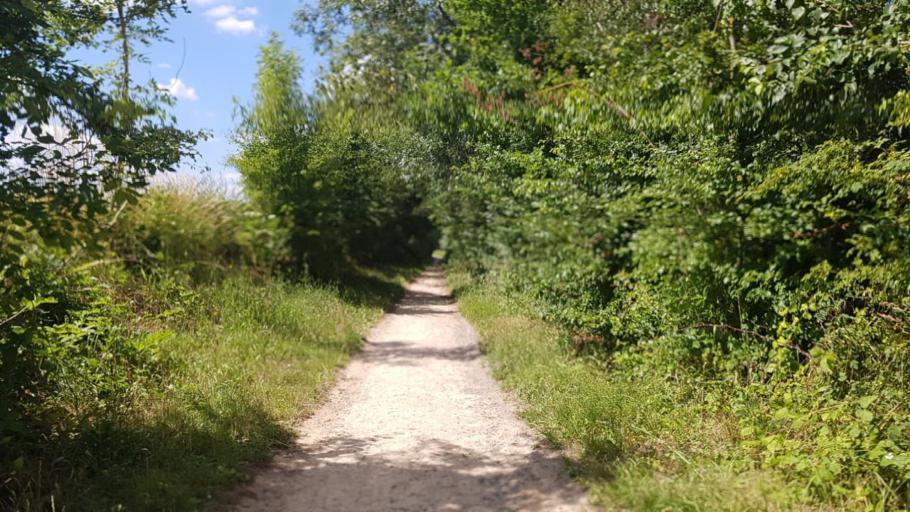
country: FR
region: Ile-de-France
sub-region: Departement de Seine-et-Marne
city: Moussy-le-Vieux
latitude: 49.0419
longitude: 2.6307
